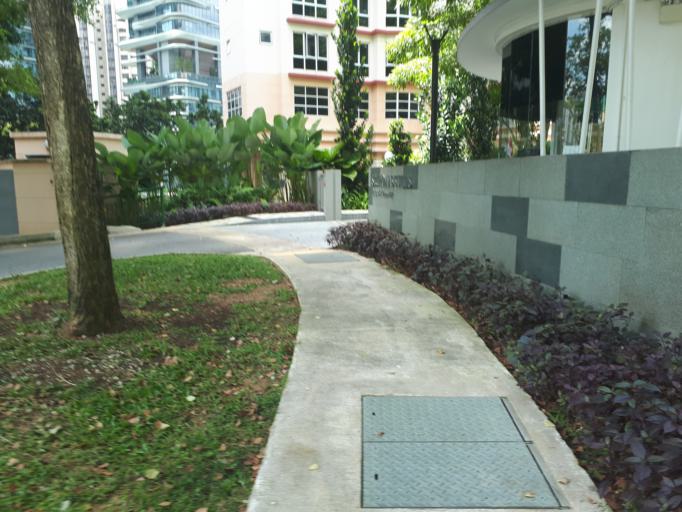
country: SG
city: Singapore
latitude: 1.2980
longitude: 103.8355
